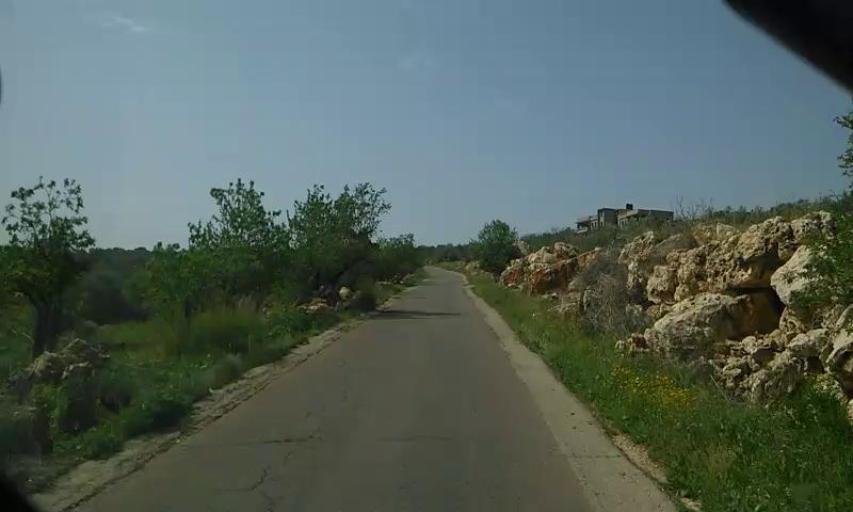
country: PS
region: West Bank
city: At Taybah
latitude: 32.4985
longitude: 35.1882
